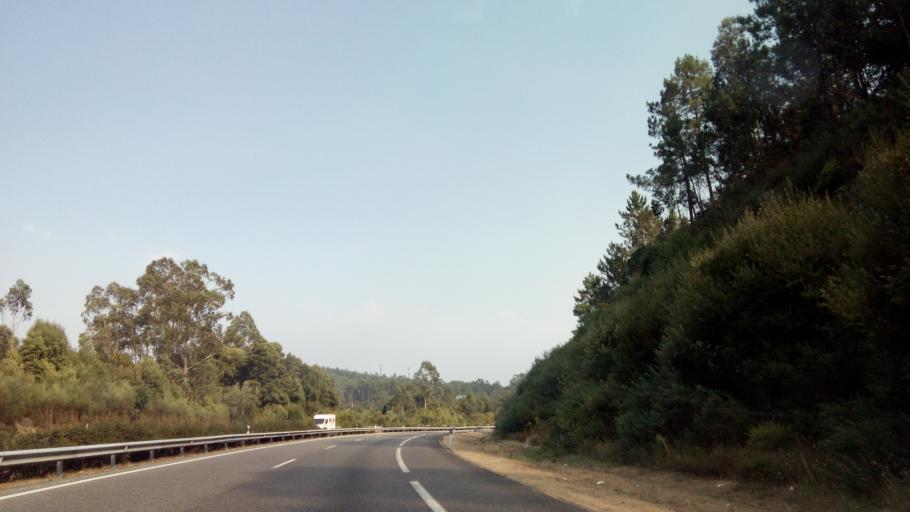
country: ES
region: Galicia
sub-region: Provincia de Pontevedra
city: Ponteareas
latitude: 42.1713
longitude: -8.5450
